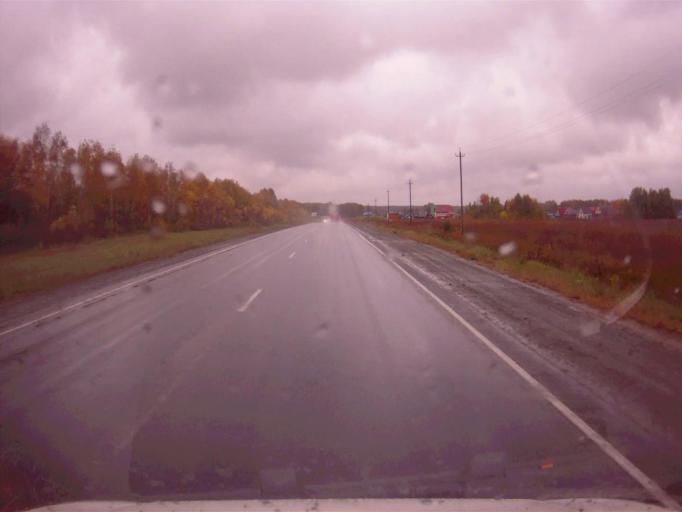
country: RU
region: Chelyabinsk
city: Argayash
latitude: 55.4055
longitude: 61.0607
